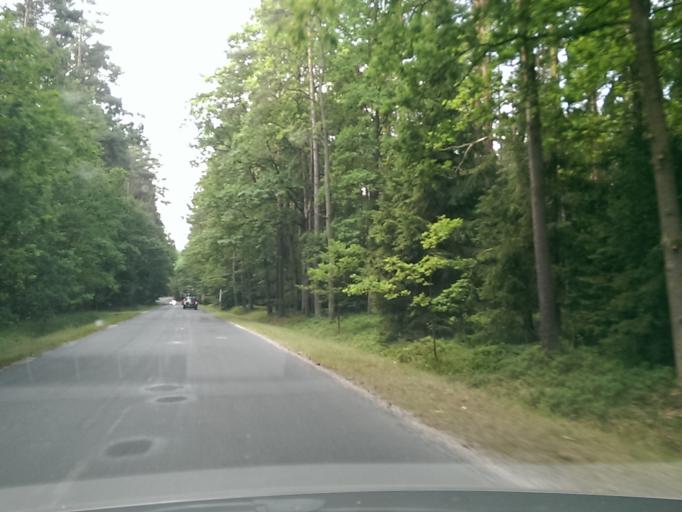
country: CZ
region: Central Bohemia
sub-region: Okres Mlada Boleslav
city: Zd'ar
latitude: 50.5094
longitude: 15.1133
